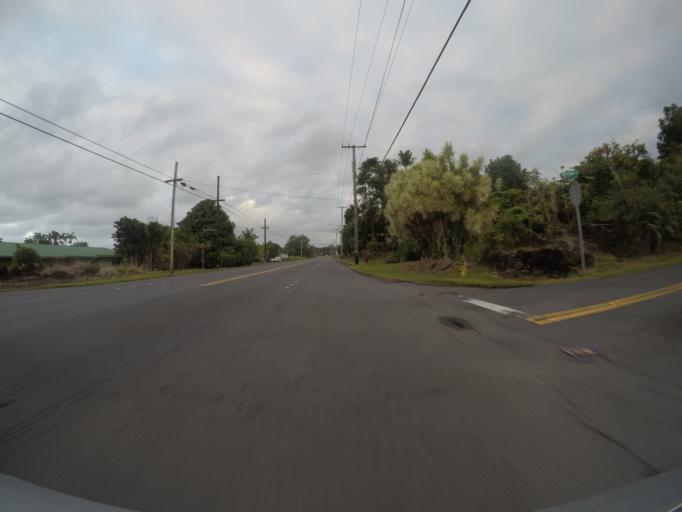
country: US
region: Hawaii
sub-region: Hawaii County
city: Hilo
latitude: 19.6798
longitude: -155.0672
